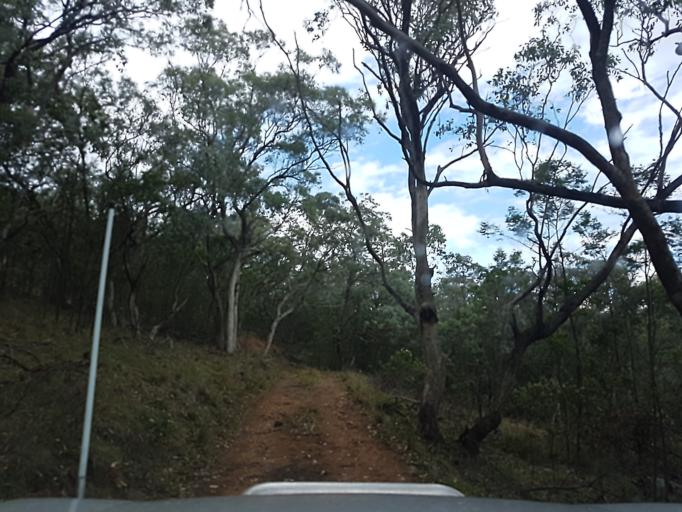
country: AU
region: New South Wales
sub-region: Snowy River
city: Jindabyne
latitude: -36.9712
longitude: 148.3939
